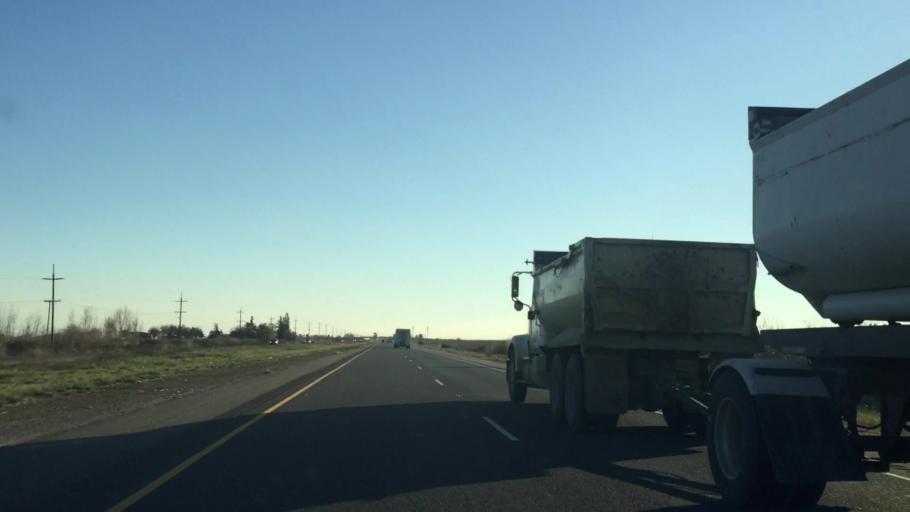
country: US
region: California
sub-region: Yuba County
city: Plumas Lake
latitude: 38.9428
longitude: -121.5440
